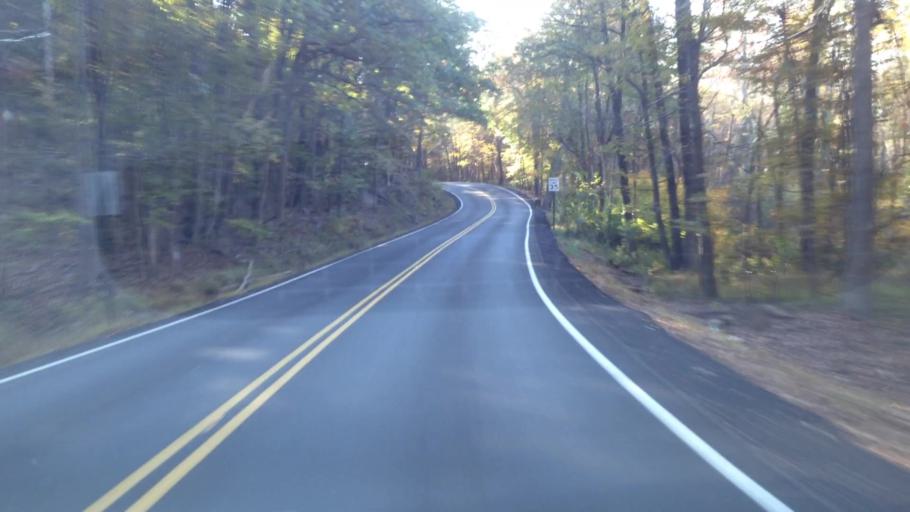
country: US
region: New York
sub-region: Ulster County
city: Tillson
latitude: 41.8237
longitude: -74.0029
